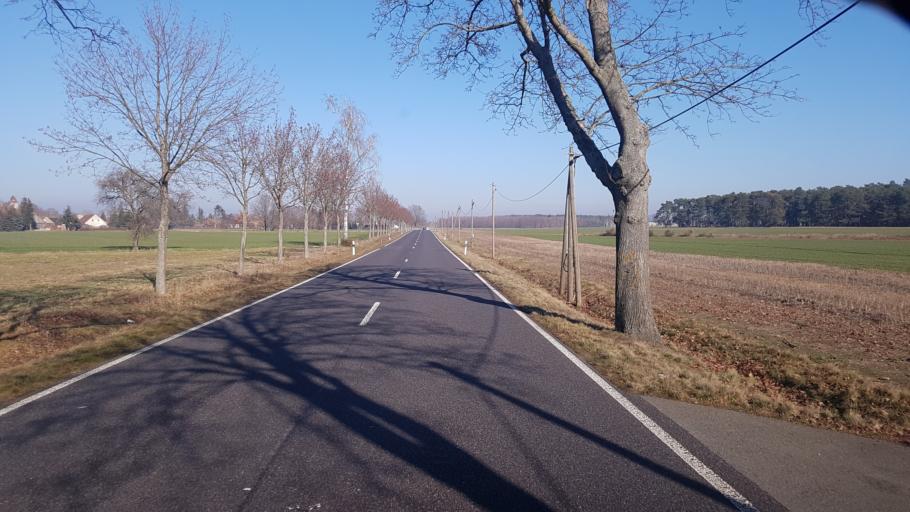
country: DE
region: Brandenburg
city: Ihlow
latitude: 51.8118
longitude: 13.3310
